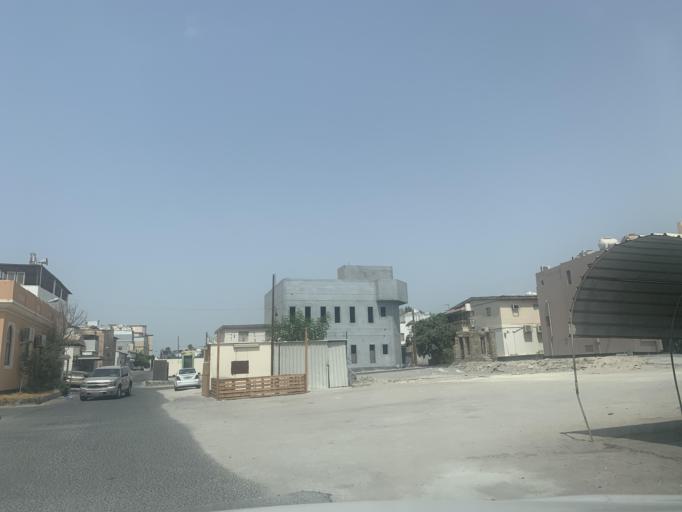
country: BH
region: Manama
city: Jidd Hafs
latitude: 26.2219
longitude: 50.4655
